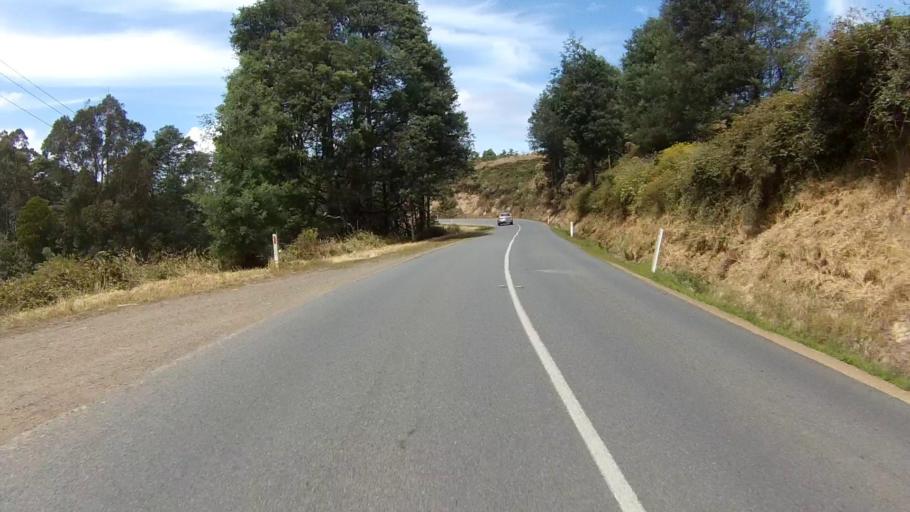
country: AU
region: Tasmania
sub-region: Kingborough
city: Kettering
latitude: -43.1053
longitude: 147.2262
